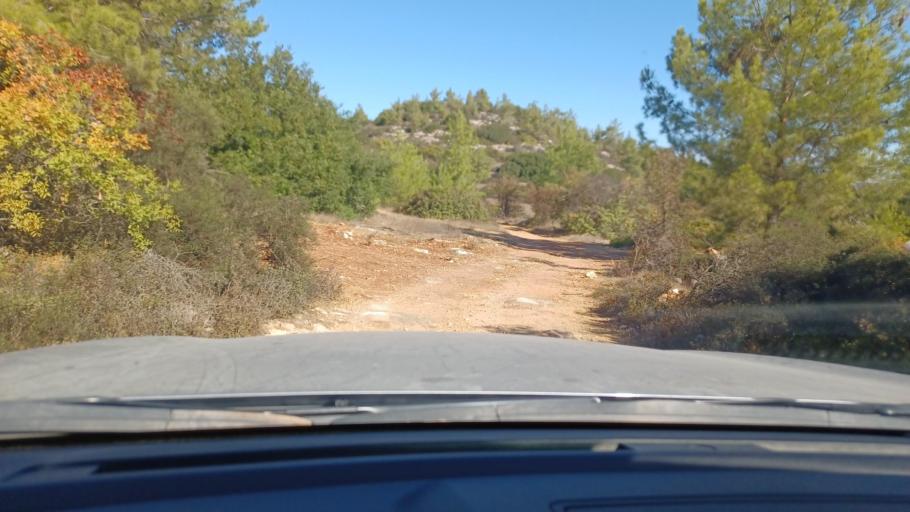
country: CY
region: Pafos
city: Polis
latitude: 34.9915
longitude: 32.5216
